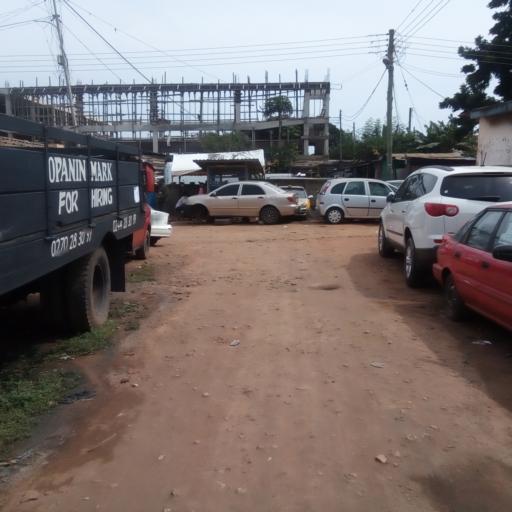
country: GH
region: Greater Accra
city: Dome
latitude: 5.6105
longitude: -0.2387
